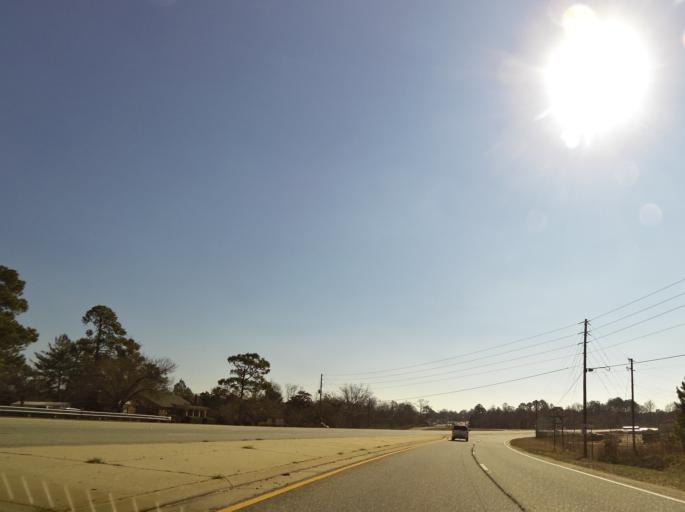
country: US
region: Georgia
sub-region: Pulaski County
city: Hawkinsville
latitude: 32.2946
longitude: -83.4843
